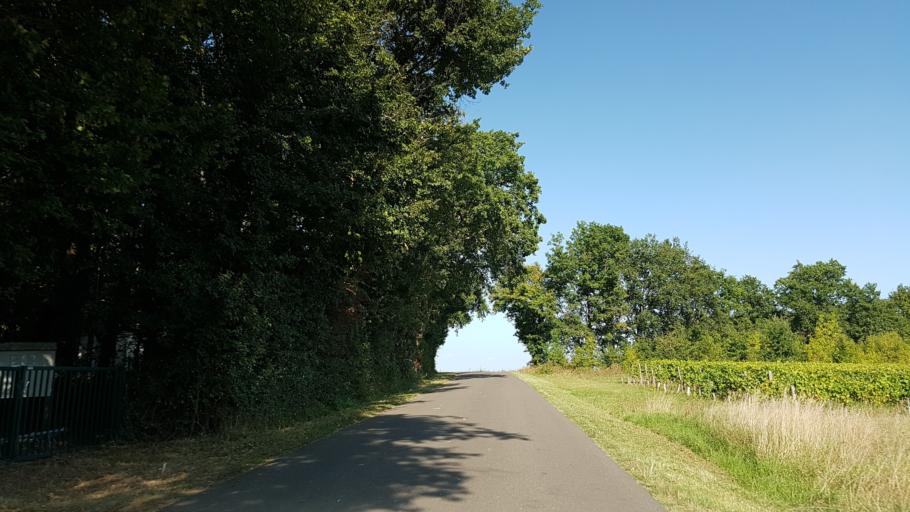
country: FR
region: Poitou-Charentes
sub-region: Departement de la Charente-Maritime
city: Breuillet
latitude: 45.7019
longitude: -1.0492
